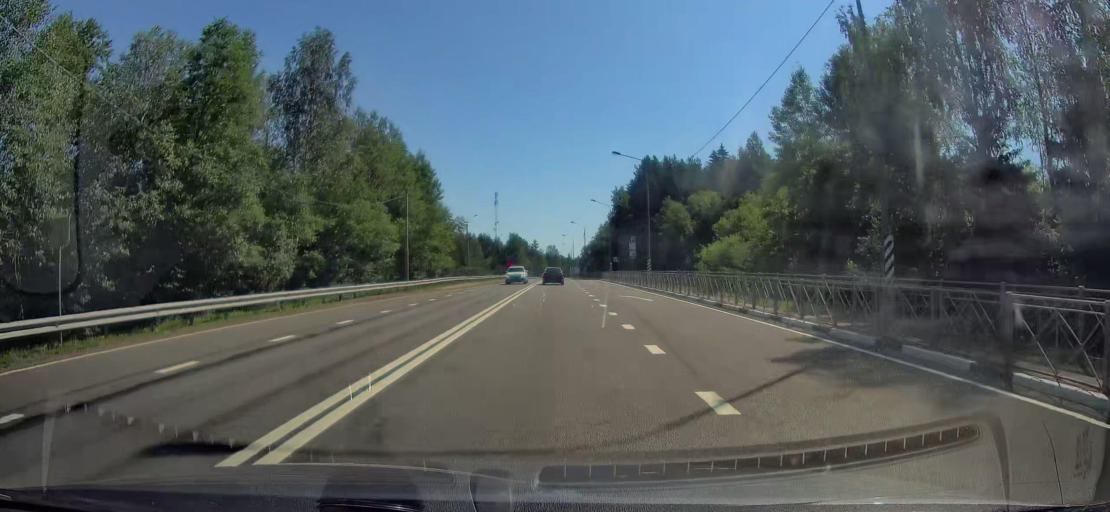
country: RU
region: Leningrad
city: Yefimovskiy
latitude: 59.3467
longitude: 34.8602
